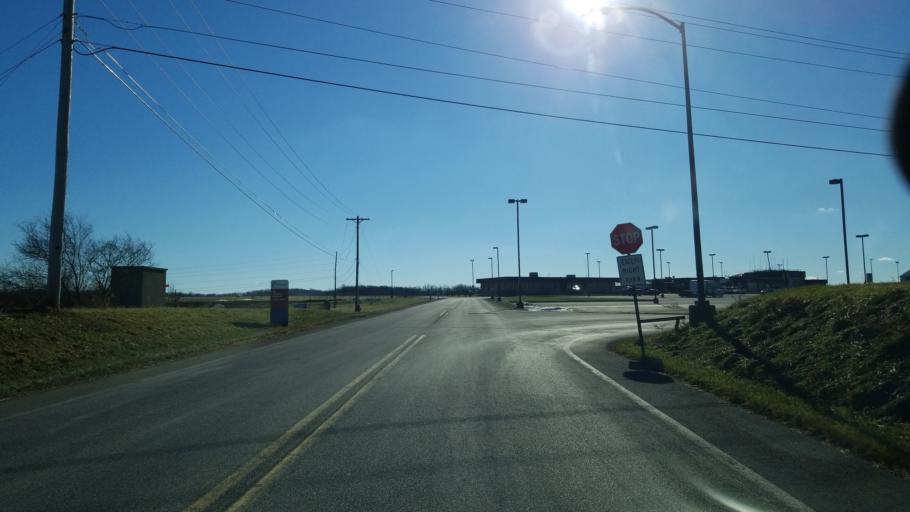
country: US
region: Pennsylvania
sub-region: Jefferson County
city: Reynoldsville
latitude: 41.1851
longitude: -78.8918
